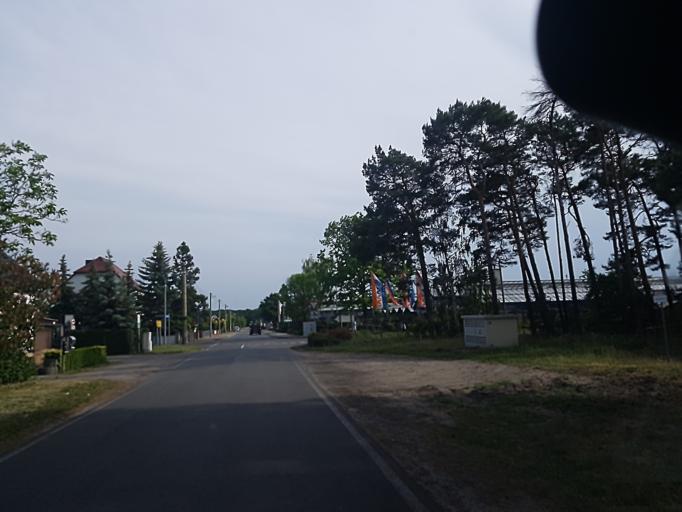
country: DE
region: Saxony-Anhalt
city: Jessen
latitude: 51.8004
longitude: 12.9542
